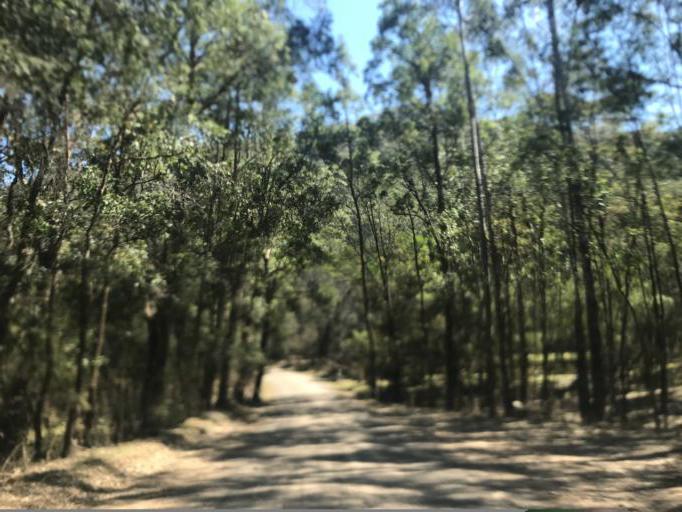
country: AU
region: New South Wales
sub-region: Wyong Shire
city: Little Jilliby
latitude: -33.1940
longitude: 151.0136
